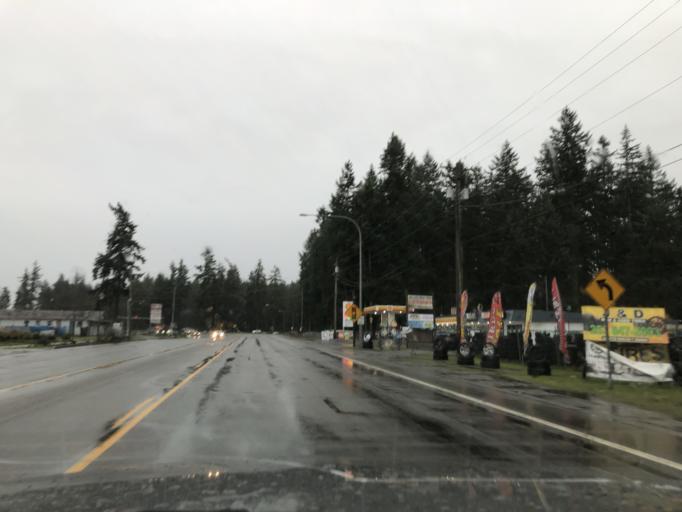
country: US
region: Washington
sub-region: Pierce County
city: Spanaway
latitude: 47.0853
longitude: -122.4353
